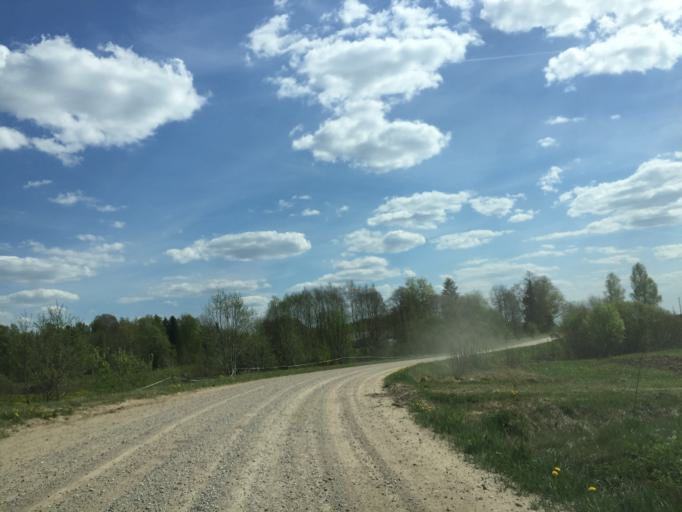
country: LV
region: Limbazu Rajons
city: Limbazi
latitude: 57.3938
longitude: 24.6475
